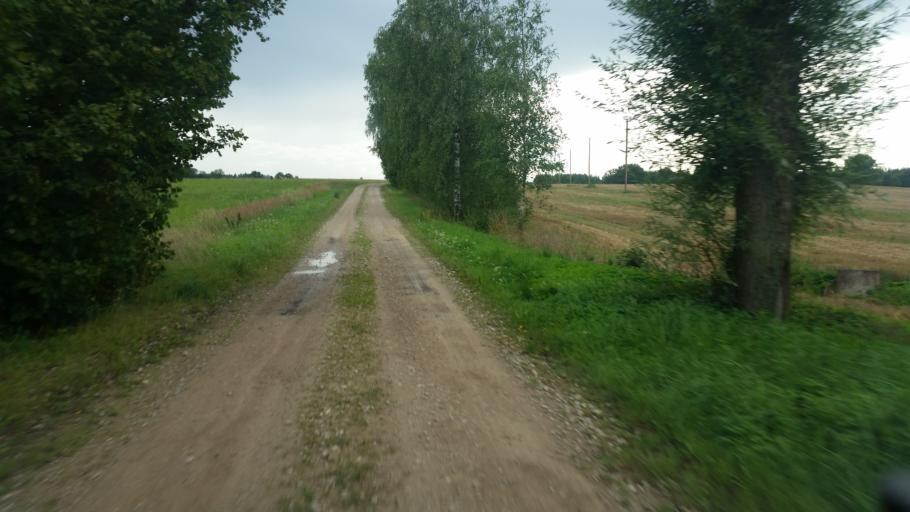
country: LV
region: Vecumnieki
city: Vecumnieki
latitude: 56.4601
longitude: 24.6636
